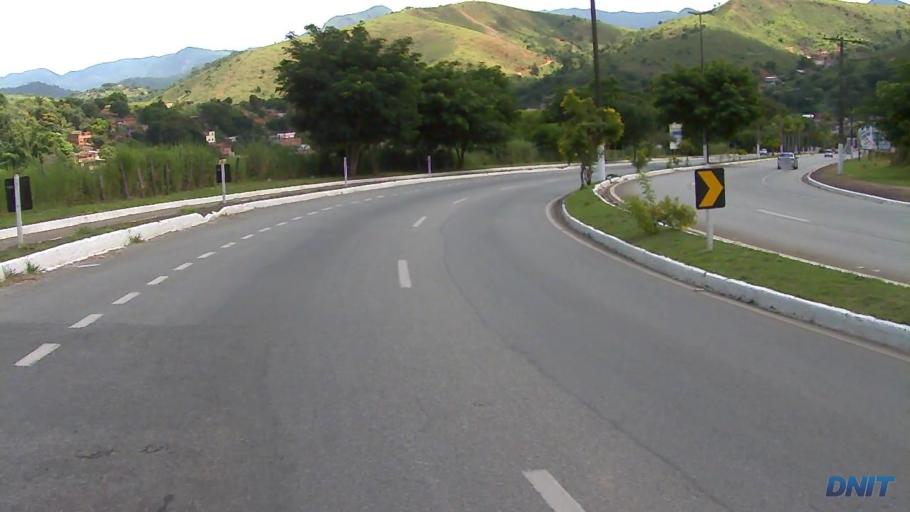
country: BR
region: Minas Gerais
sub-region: Coronel Fabriciano
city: Coronel Fabriciano
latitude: -19.5057
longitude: -42.5932
